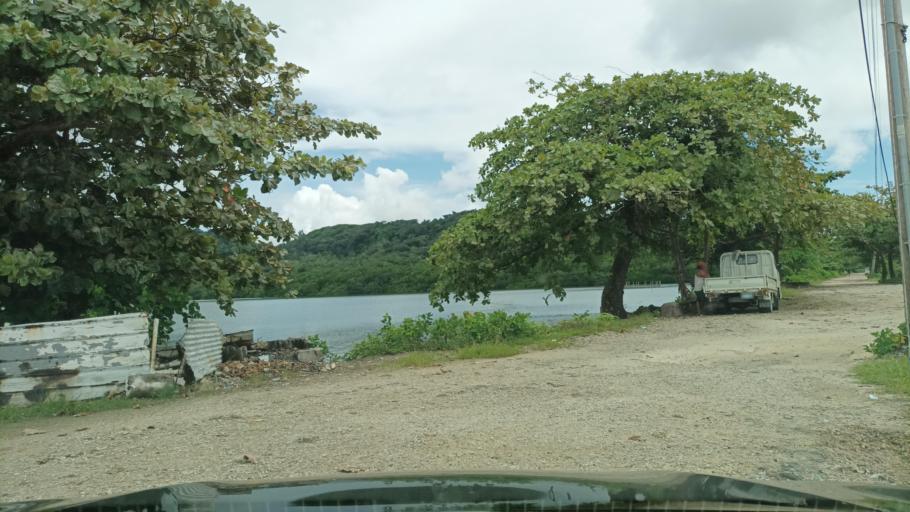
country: FM
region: Pohnpei
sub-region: Kolonia Municipality
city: Kolonia
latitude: 6.9796
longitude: 158.2261
